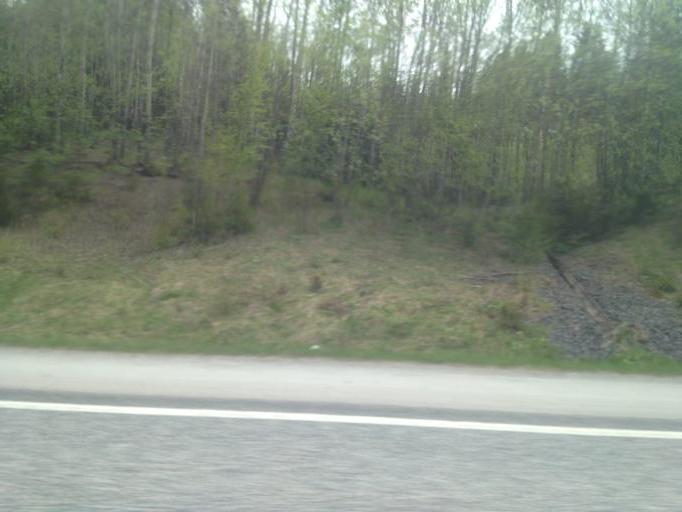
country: FI
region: Uusimaa
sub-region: Helsinki
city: Nurmijaervi
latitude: 60.4015
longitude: 24.8183
